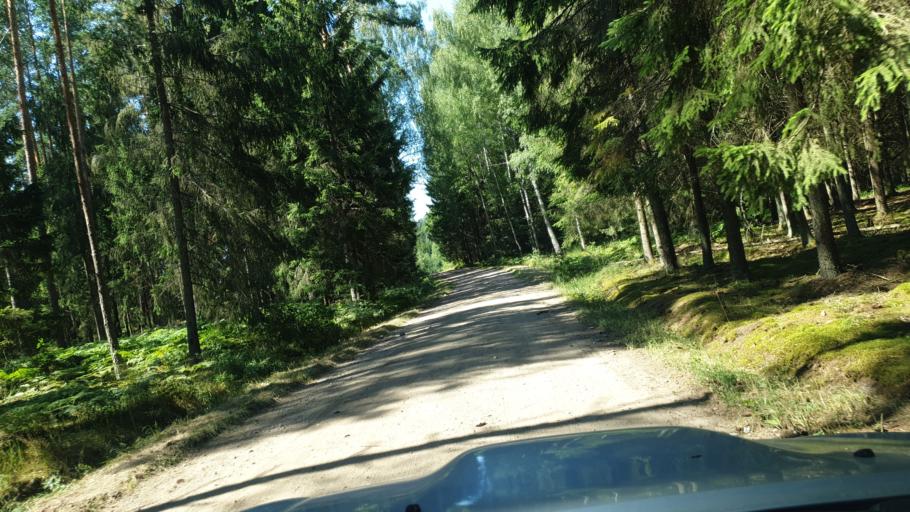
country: LT
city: Sirvintos
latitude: 54.9069
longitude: 24.9447
